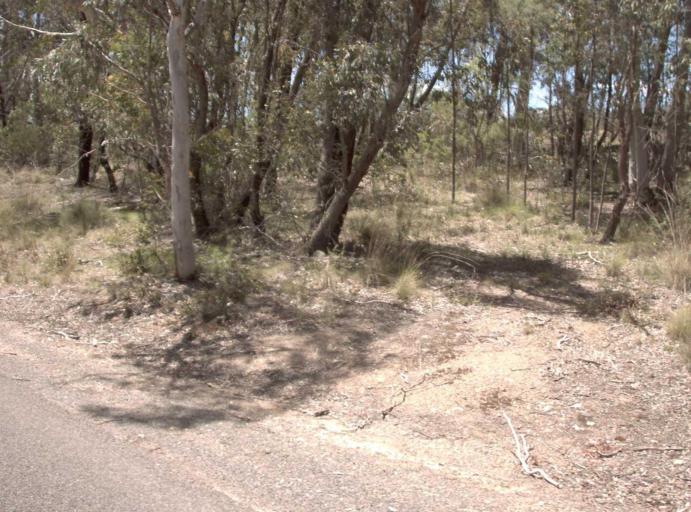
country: AU
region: New South Wales
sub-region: Snowy River
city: Jindabyne
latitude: -37.0778
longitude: 148.2823
